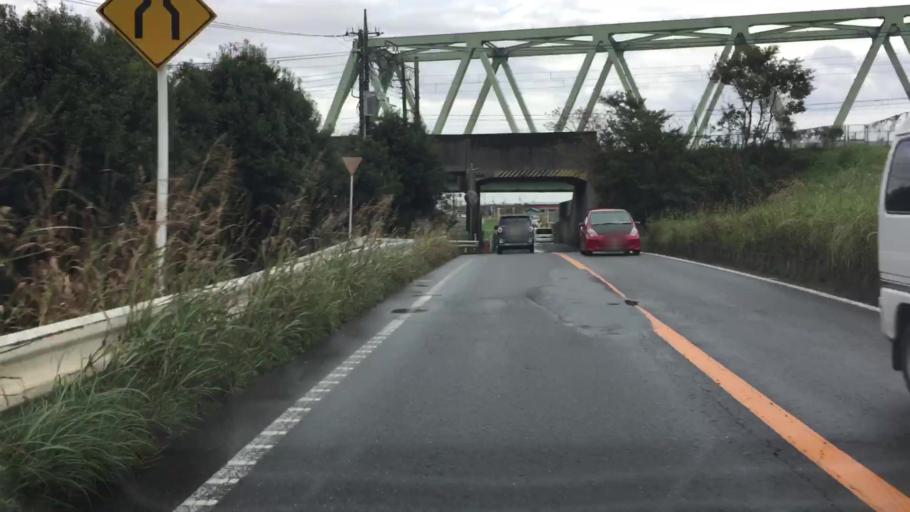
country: JP
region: Ibaraki
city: Toride
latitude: 35.8845
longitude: 140.0567
